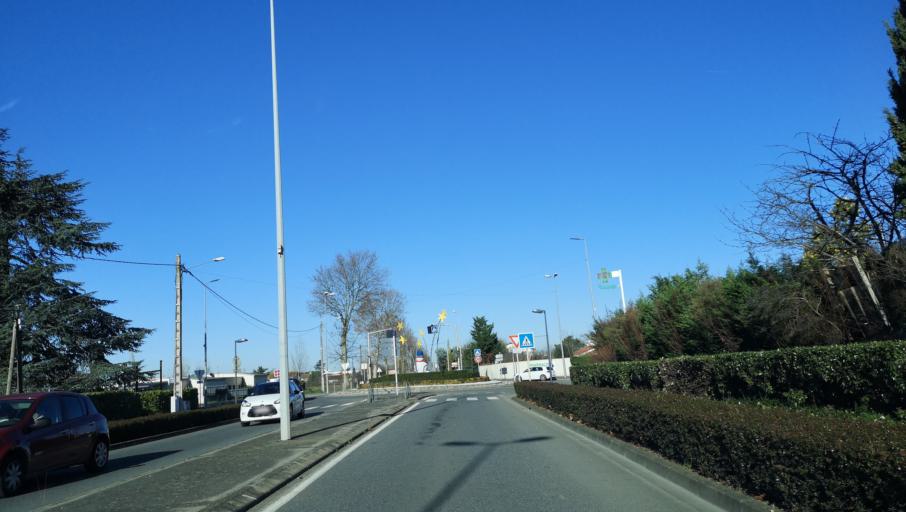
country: FR
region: Midi-Pyrenees
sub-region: Departement de la Haute-Garonne
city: Beauzelle
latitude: 43.6634
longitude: 1.3726
